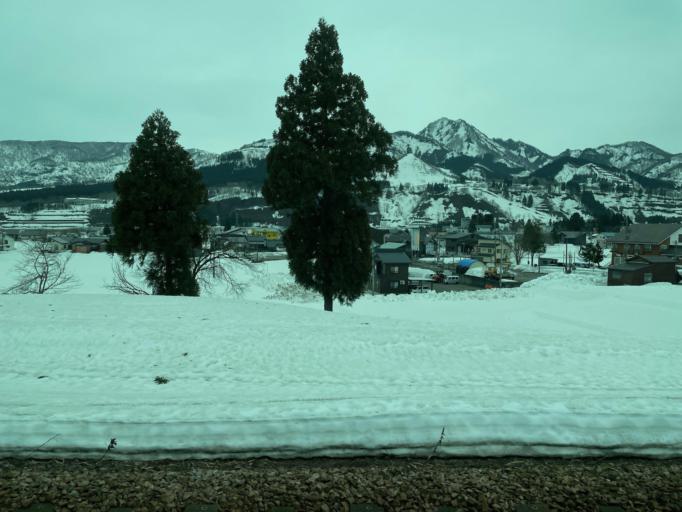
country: JP
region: Niigata
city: Shiozawa
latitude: 36.9826
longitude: 138.8013
